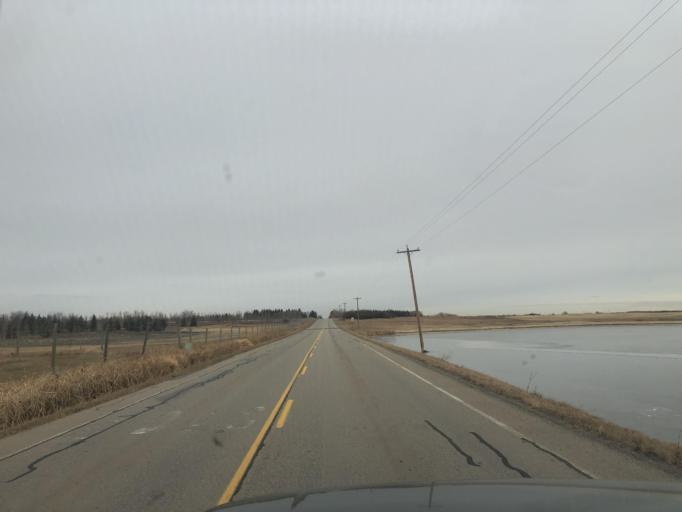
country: CA
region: Alberta
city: Chestermere
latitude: 50.9814
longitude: -113.8654
